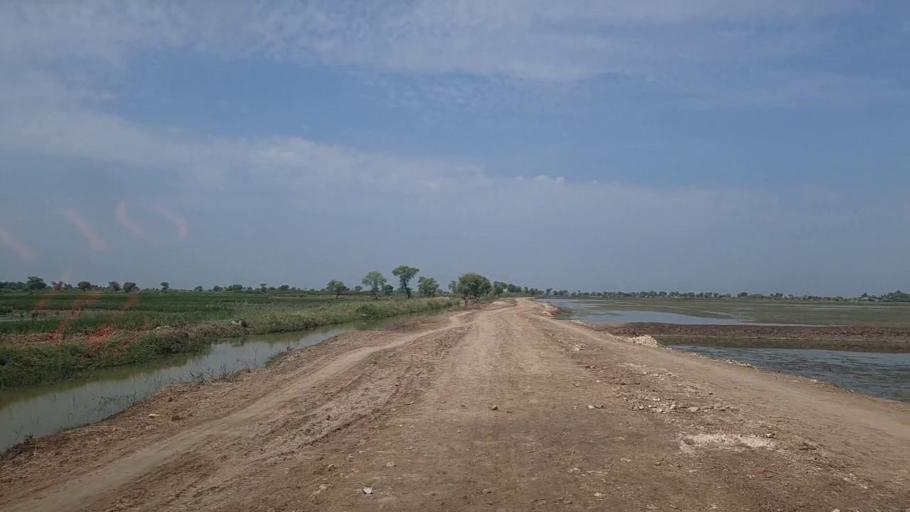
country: PK
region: Sindh
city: Thul
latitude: 28.3012
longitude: 68.6768
